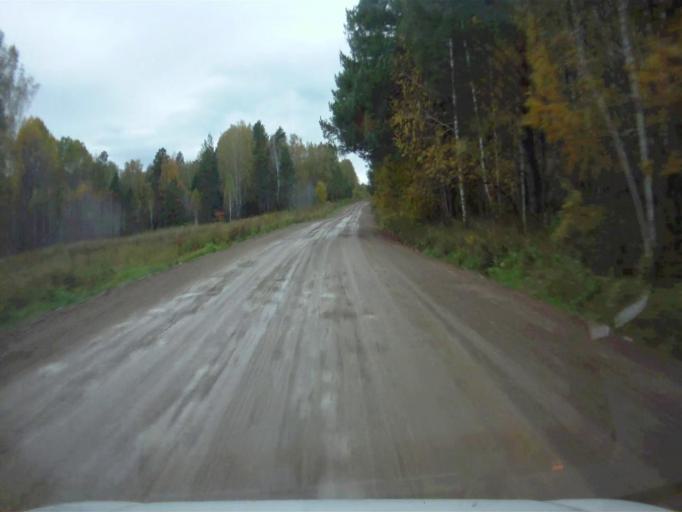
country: RU
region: Chelyabinsk
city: Nyazepetrovsk
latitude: 56.0968
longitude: 59.3978
